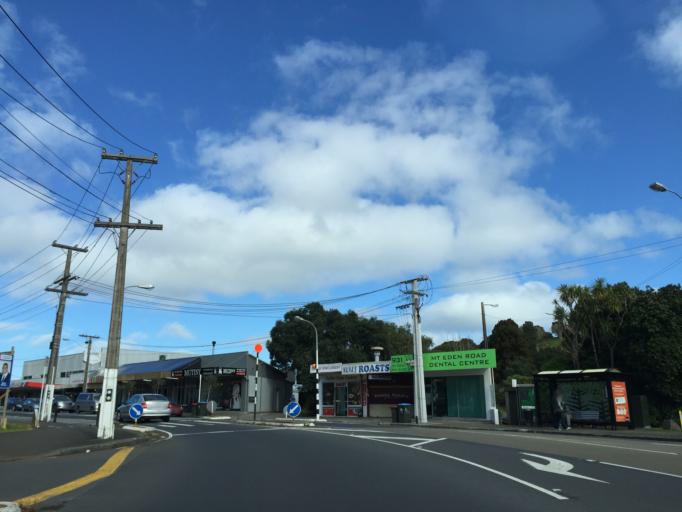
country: NZ
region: Auckland
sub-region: Auckland
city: Auckland
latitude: -36.8994
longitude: 174.7568
